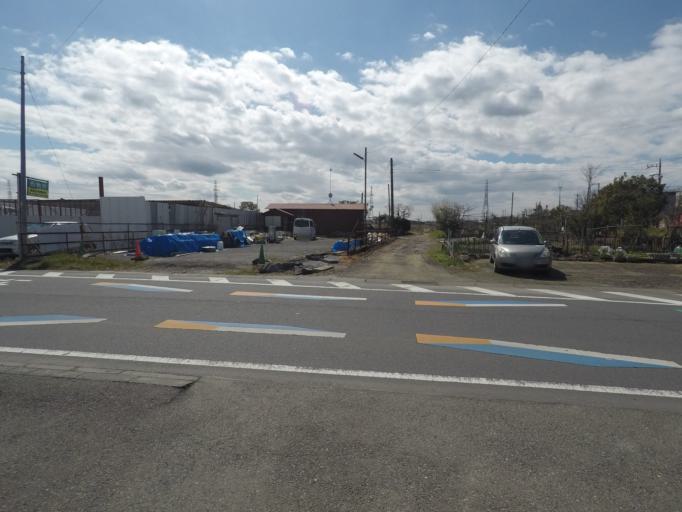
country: JP
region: Ibaraki
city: Fujishiro
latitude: 35.9361
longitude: 140.1239
